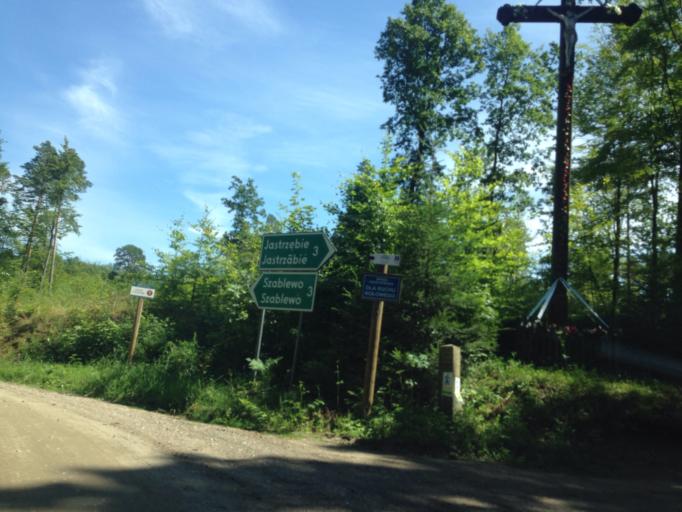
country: PL
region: Pomeranian Voivodeship
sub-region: Powiat koscierski
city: Dziemiany
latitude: 53.9967
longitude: 17.7821
